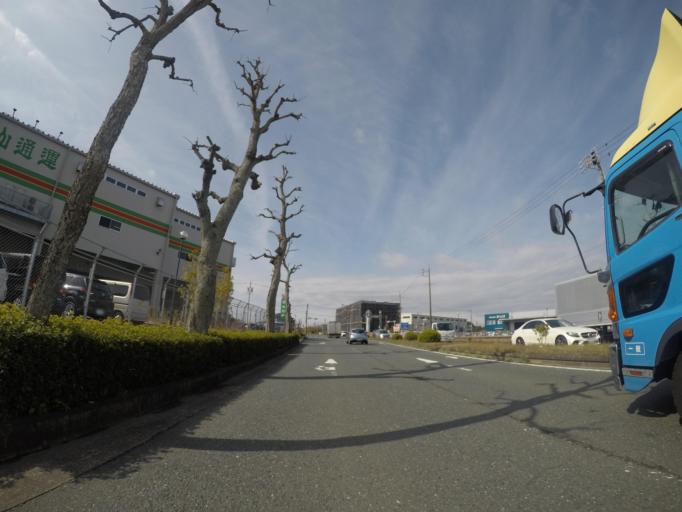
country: JP
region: Shizuoka
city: Hamamatsu
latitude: 34.7743
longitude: 137.6947
